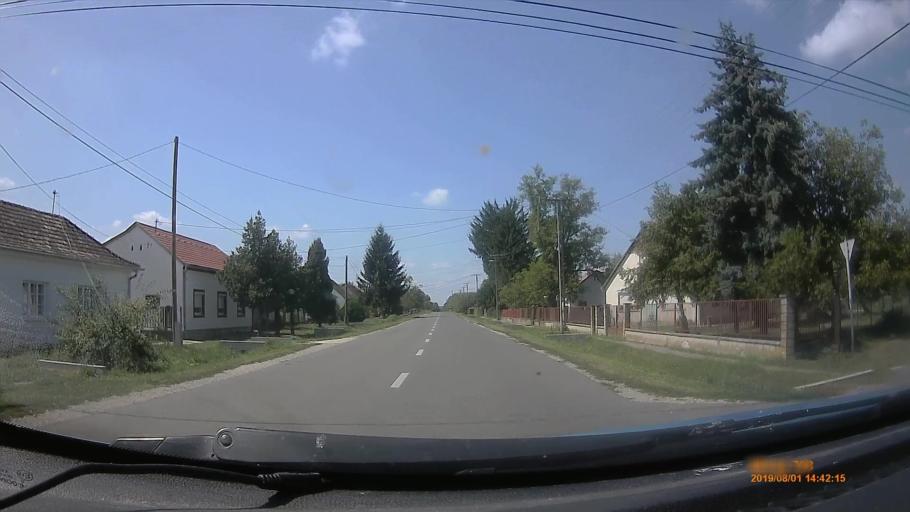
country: HR
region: Osjecko-Baranjska
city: Viljevo
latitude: 45.8275
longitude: 18.0973
